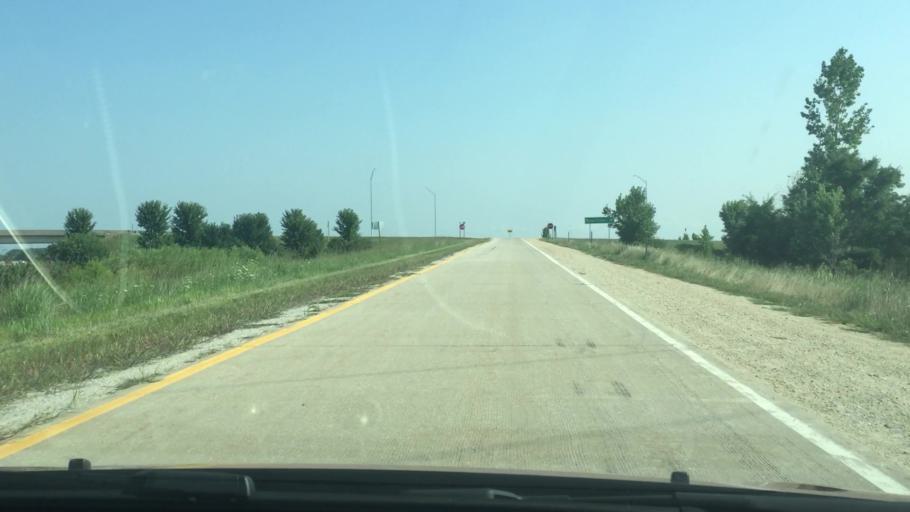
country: US
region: Iowa
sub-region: Scott County
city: Blue Grass
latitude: 41.5126
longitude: -90.7564
